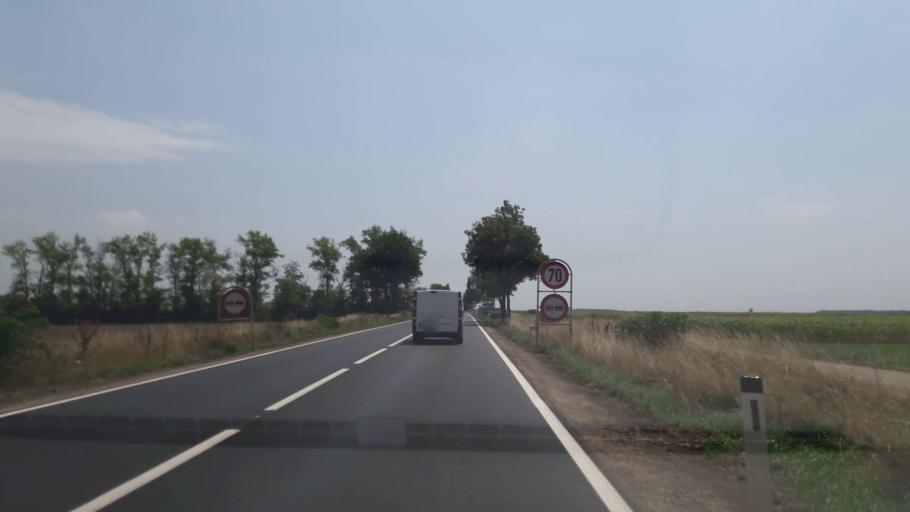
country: AT
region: Lower Austria
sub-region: Politischer Bezirk Wien-Umgebung
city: Rauchenwarth
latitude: 48.1080
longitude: 16.5279
